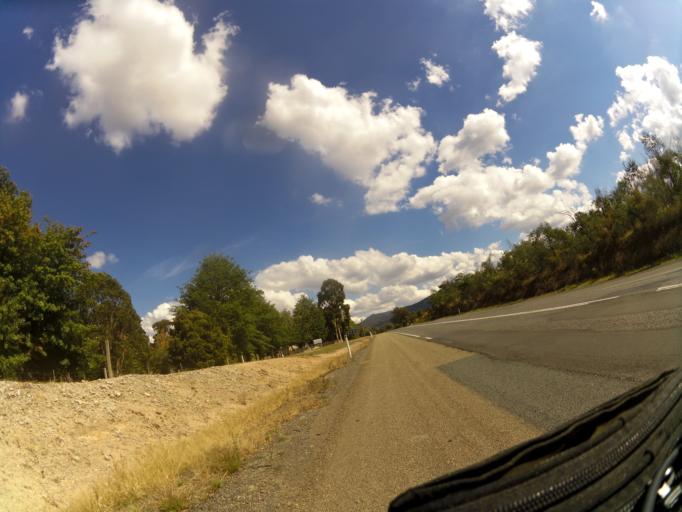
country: AU
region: Victoria
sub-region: Mansfield
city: Mansfield
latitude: -36.8539
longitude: 146.0057
